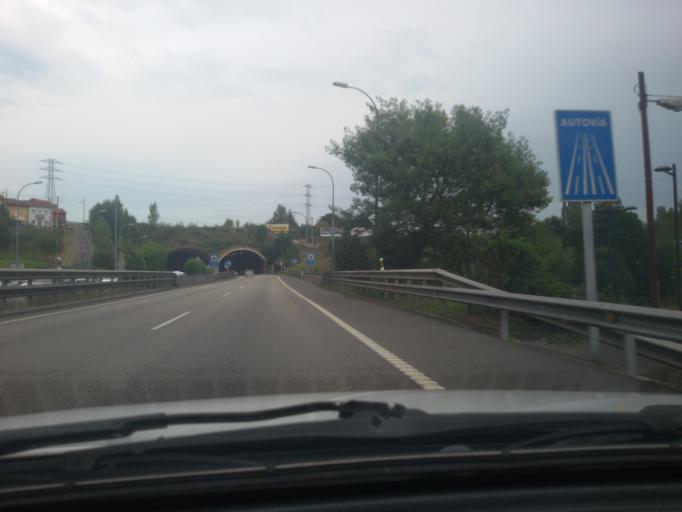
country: ES
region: Asturias
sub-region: Province of Asturias
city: Oviedo
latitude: 43.3736
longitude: -5.8446
